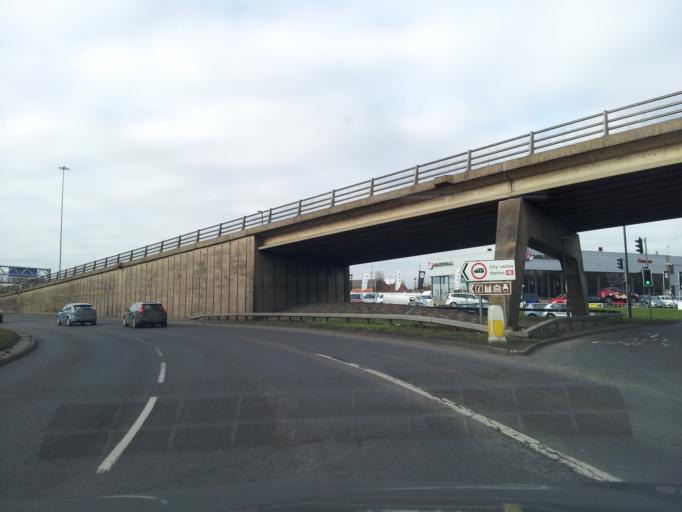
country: GB
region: England
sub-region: Derby
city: Derby
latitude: 52.9246
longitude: -1.4627
